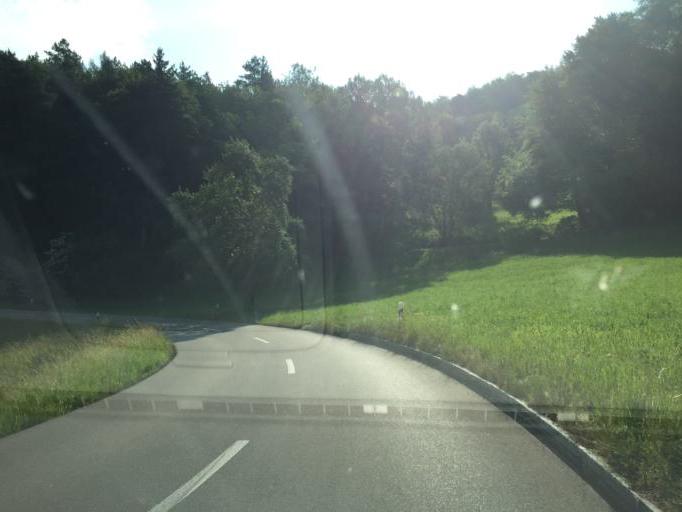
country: CH
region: Zurich
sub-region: Bezirk Buelach
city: Rorbas
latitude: 47.5581
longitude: 8.5666
